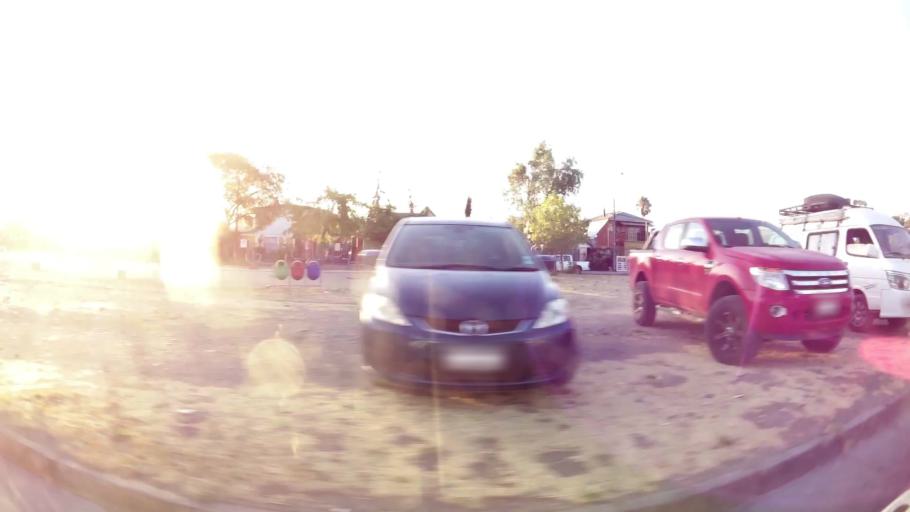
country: CL
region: Maule
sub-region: Provincia de Talca
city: Talca
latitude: -35.4474
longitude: -71.6696
